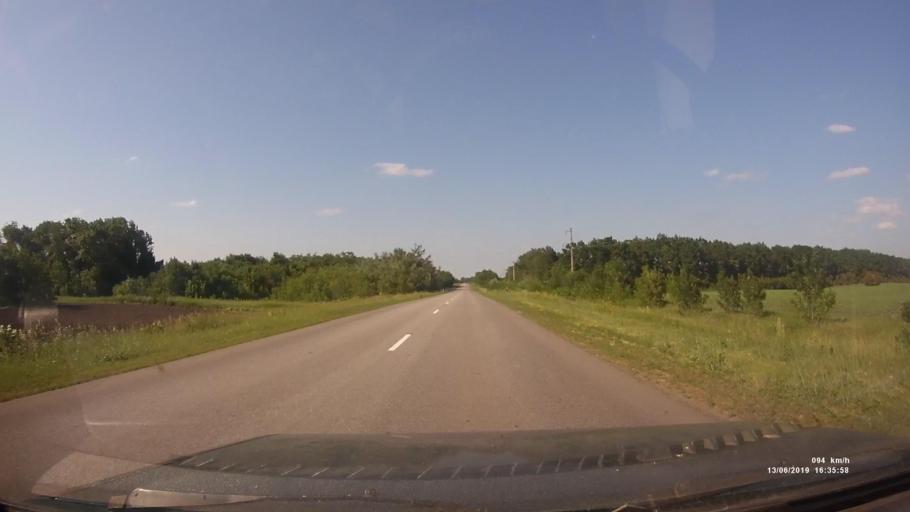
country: RU
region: Rostov
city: Kazanskaya
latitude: 49.8888
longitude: 41.3023
